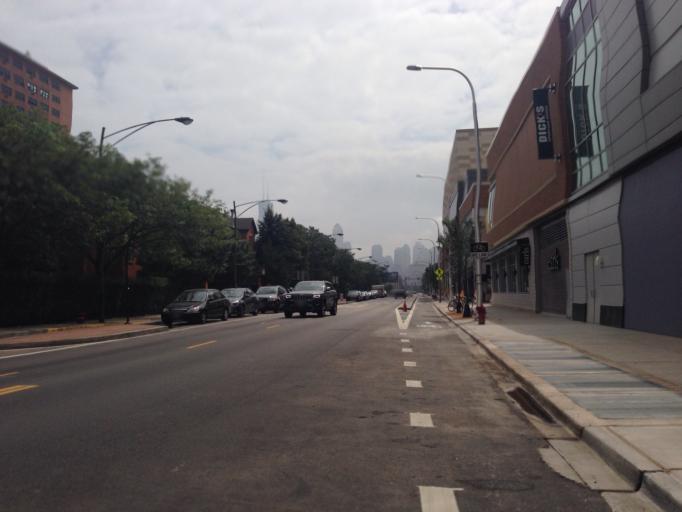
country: US
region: Illinois
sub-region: Cook County
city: Chicago
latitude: 41.9095
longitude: -87.6475
